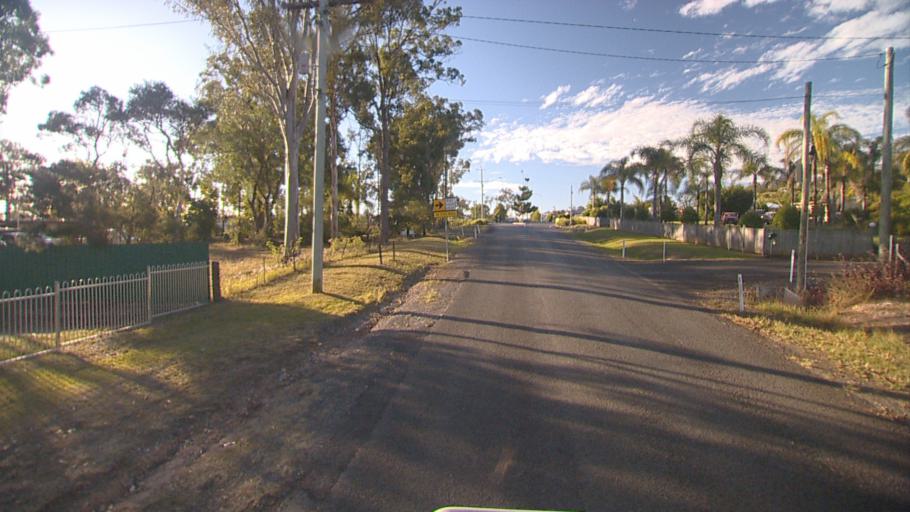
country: AU
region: Queensland
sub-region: Logan
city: Waterford West
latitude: -27.7208
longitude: 153.1540
